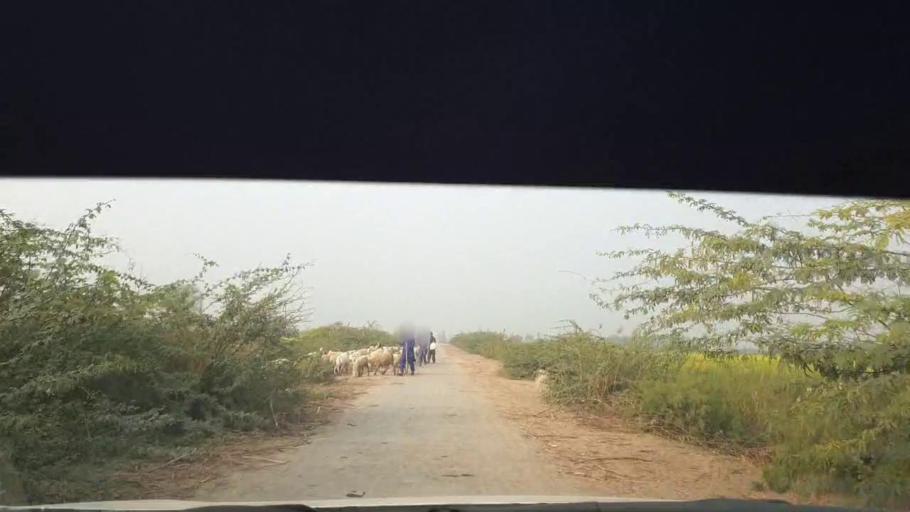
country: PK
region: Sindh
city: Berani
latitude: 25.8111
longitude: 68.8820
